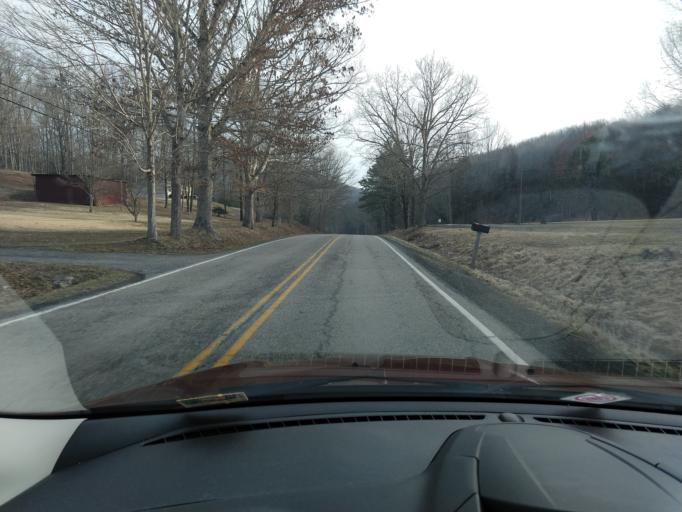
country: US
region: Virginia
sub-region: Highland County
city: Monterey
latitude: 38.4569
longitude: -79.5293
